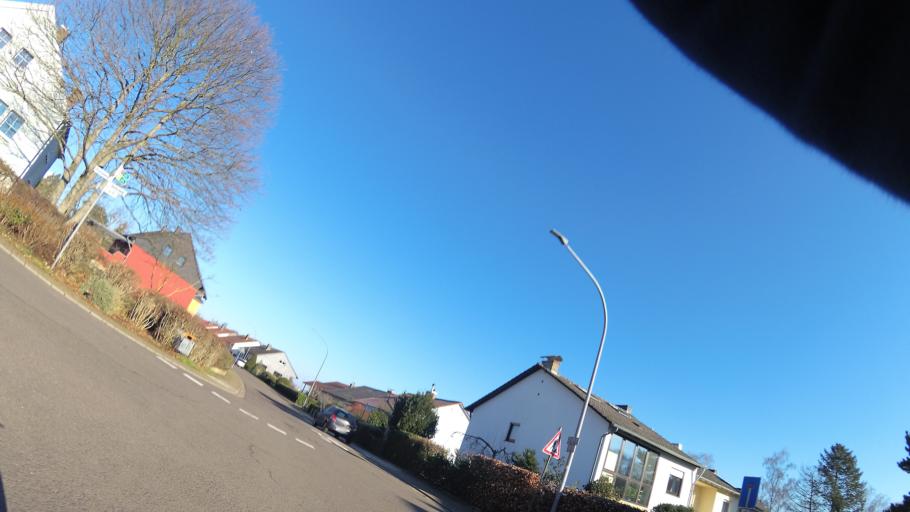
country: DE
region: Saarland
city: Saarlouis
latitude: 49.2987
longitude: 6.7364
